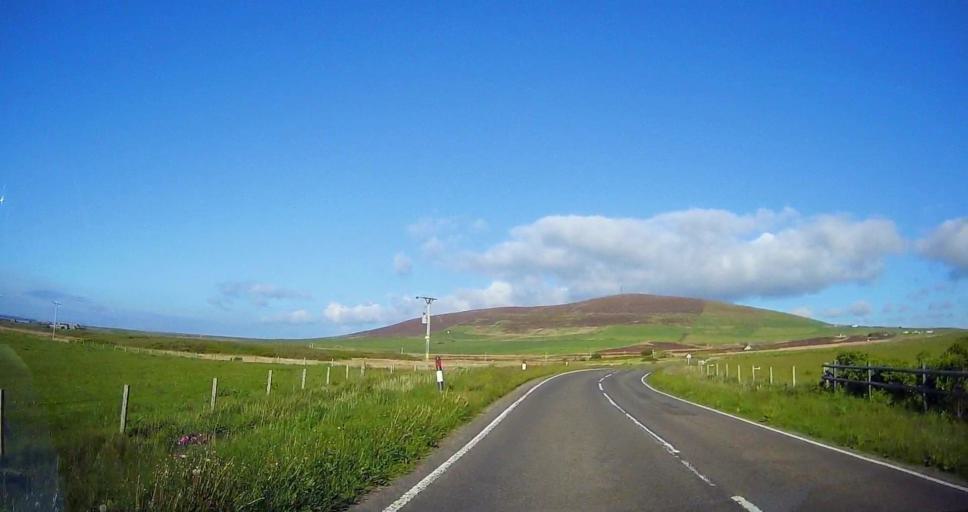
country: GB
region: Scotland
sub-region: Orkney Islands
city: Orkney
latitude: 58.9885
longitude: -3.0636
